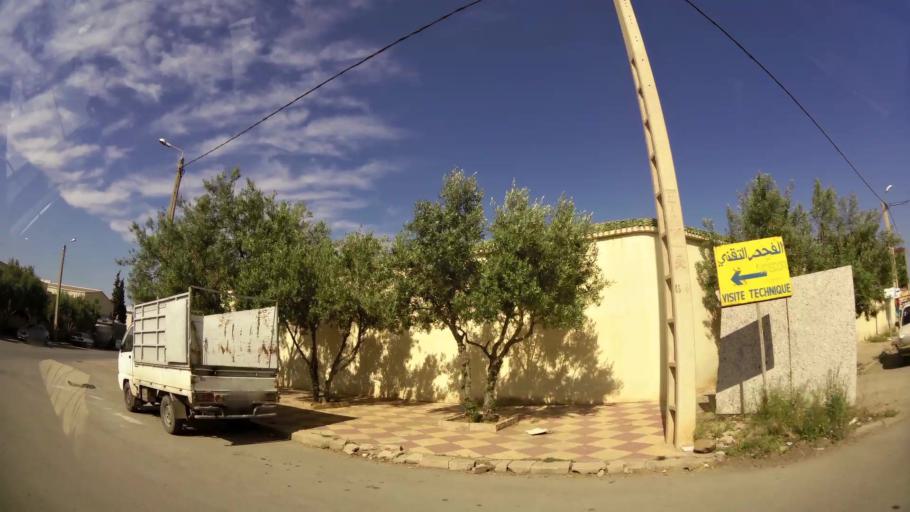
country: MA
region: Oriental
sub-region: Oujda-Angad
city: Oujda
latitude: 34.7019
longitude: -1.8921
